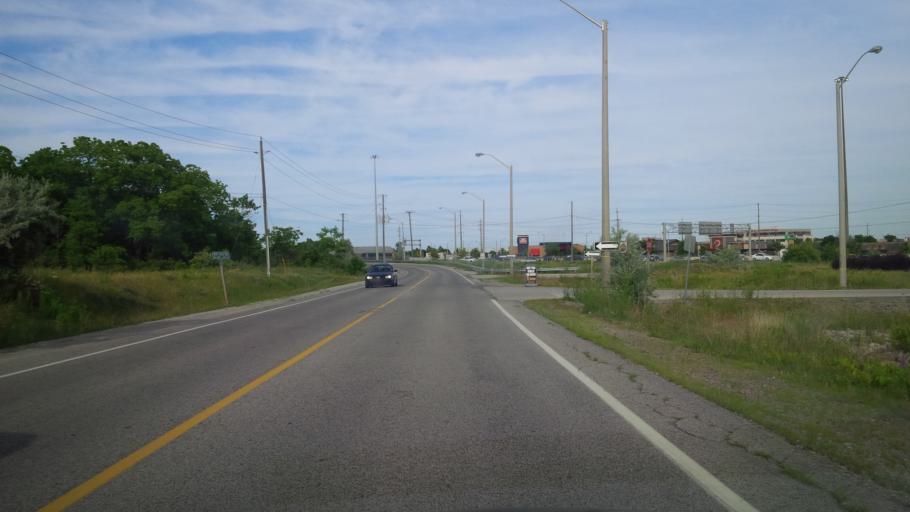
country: CA
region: Ontario
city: Burlington
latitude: 43.3551
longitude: -79.8031
